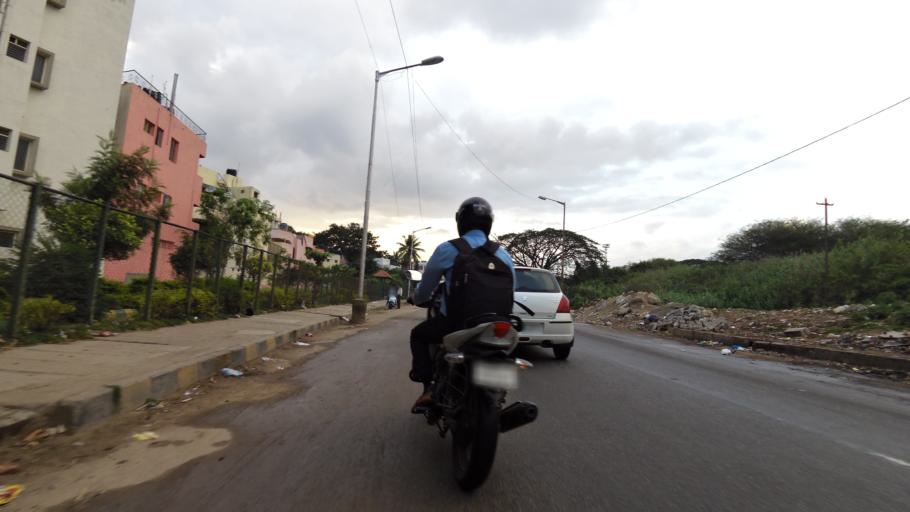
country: IN
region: Karnataka
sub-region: Bangalore Urban
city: Bangalore
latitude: 13.0015
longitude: 77.6392
